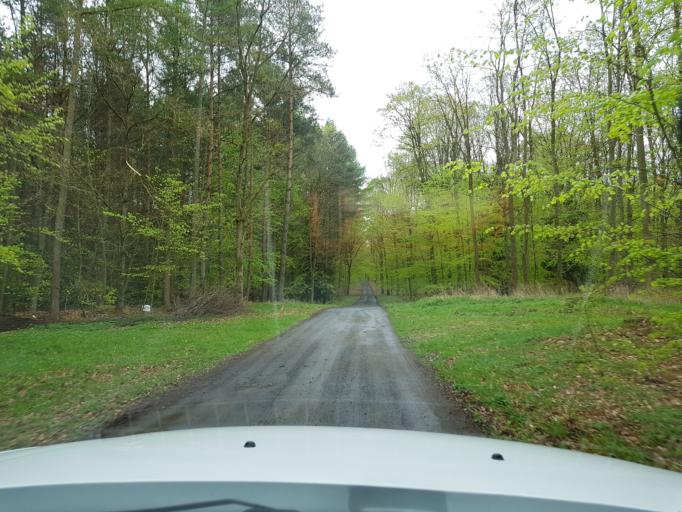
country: PL
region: West Pomeranian Voivodeship
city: Trzcinsko Zdroj
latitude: 52.9939
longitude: 14.6601
